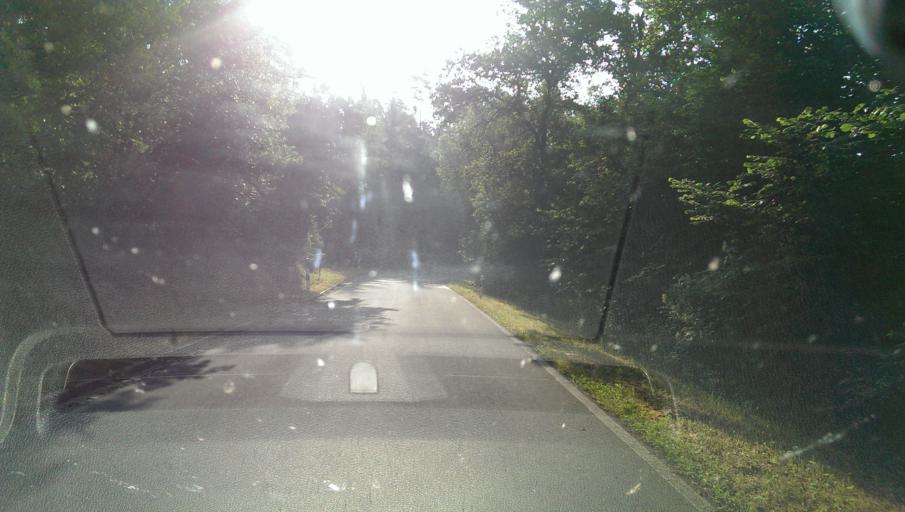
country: DE
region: Thuringia
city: Rottenbach
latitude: 50.7051
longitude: 11.1895
